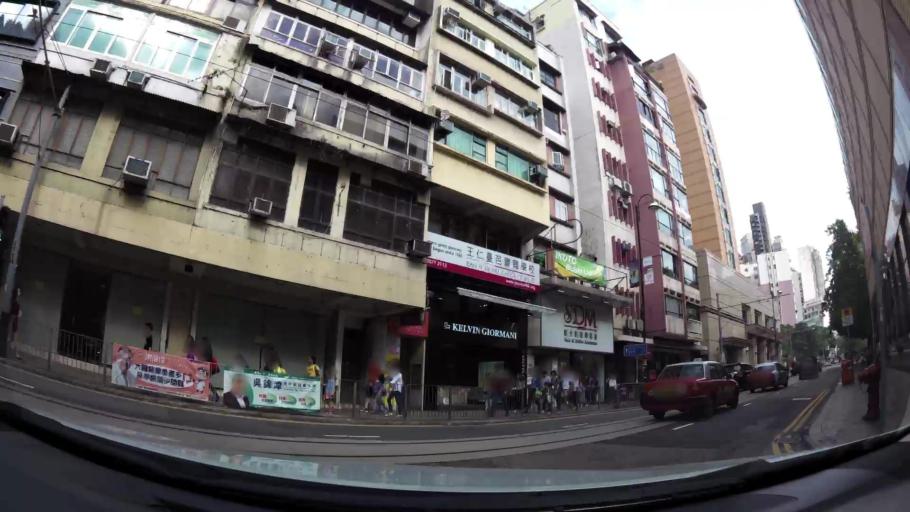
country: HK
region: Wanchai
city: Wan Chai
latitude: 22.2758
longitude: 114.1827
